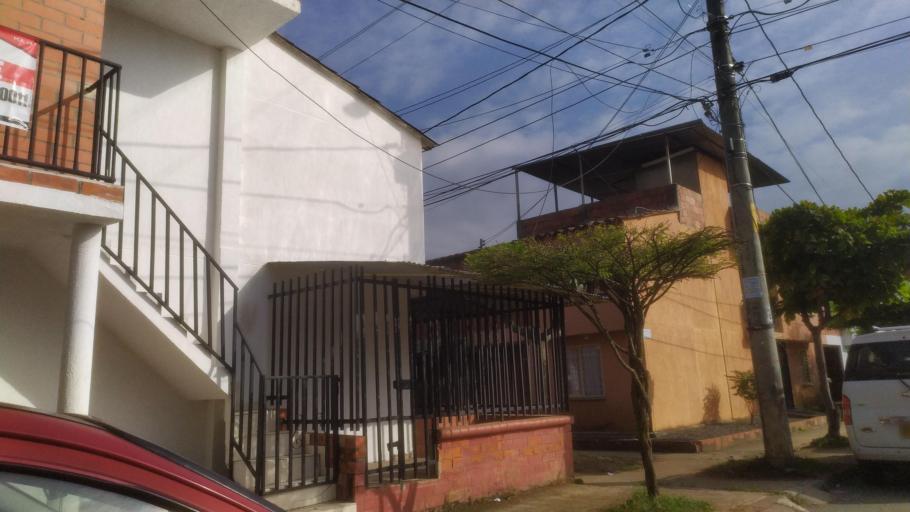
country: CO
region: Valle del Cauca
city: Jamundi
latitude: 3.2401
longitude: -76.5113
